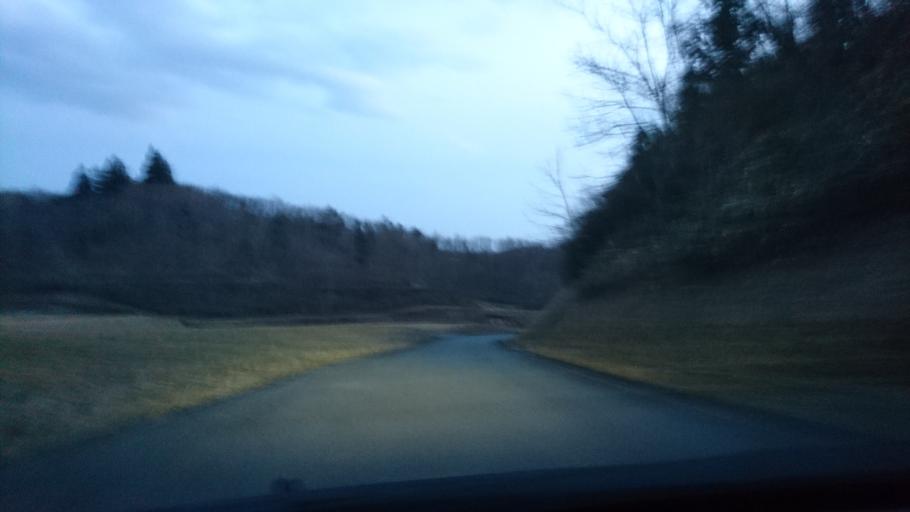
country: JP
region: Iwate
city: Ichinoseki
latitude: 38.9062
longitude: 141.3481
